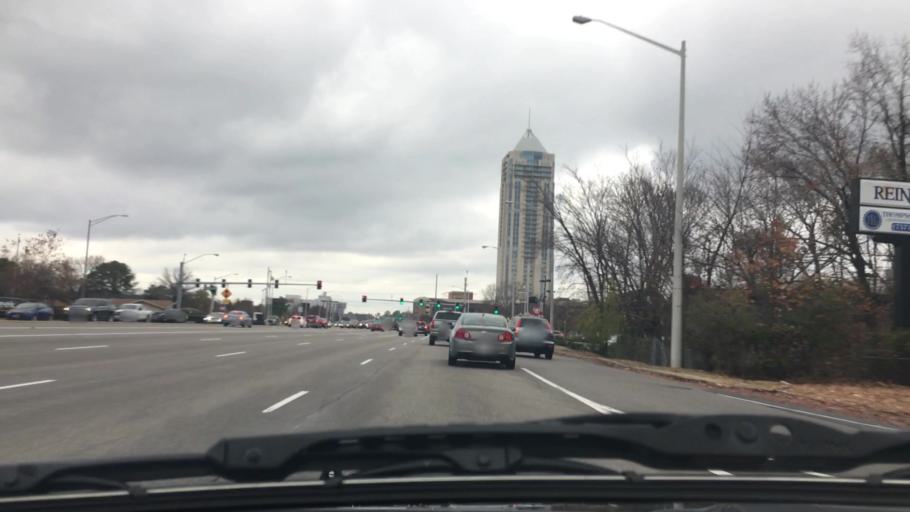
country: US
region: Virginia
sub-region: City of Chesapeake
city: Chesapeake
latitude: 36.8361
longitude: -76.1371
